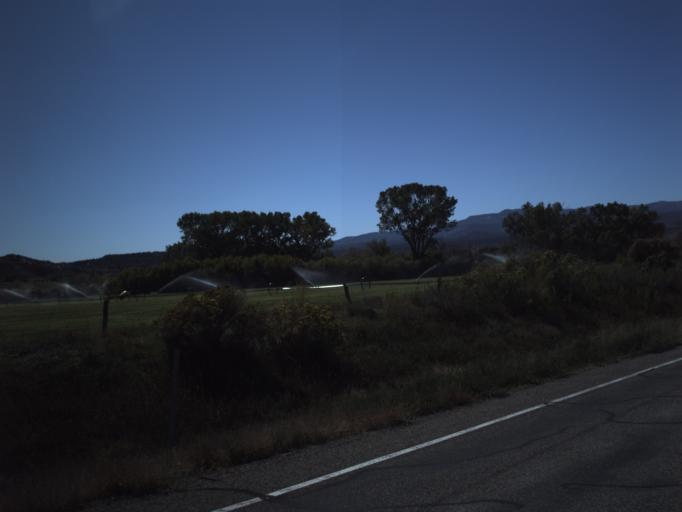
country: US
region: Utah
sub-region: Garfield County
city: Panguitch
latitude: 37.5626
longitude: -111.9985
